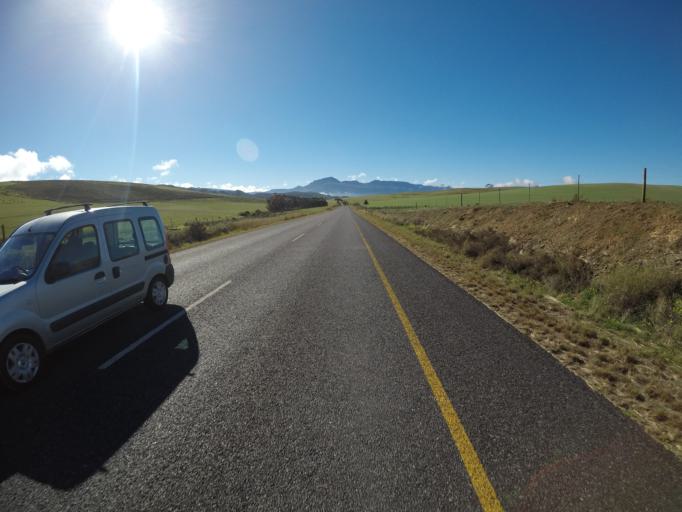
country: ZA
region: Western Cape
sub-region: Overberg District Municipality
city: Caledon
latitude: -34.1179
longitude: 19.5198
